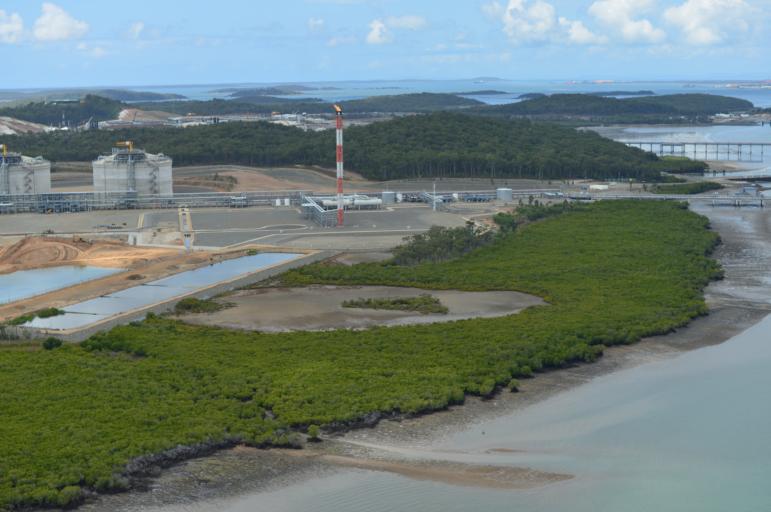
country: AU
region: Queensland
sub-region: Gladstone
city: Gladstone
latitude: -23.7691
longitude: 151.1869
